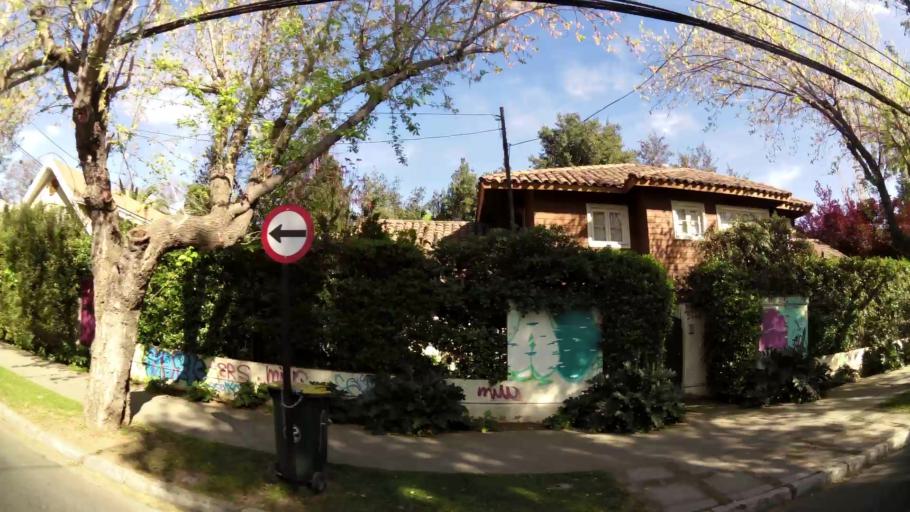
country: CL
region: Santiago Metropolitan
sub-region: Provincia de Santiago
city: Villa Presidente Frei, Nunoa, Santiago, Chile
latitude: -33.4319
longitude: -70.5600
